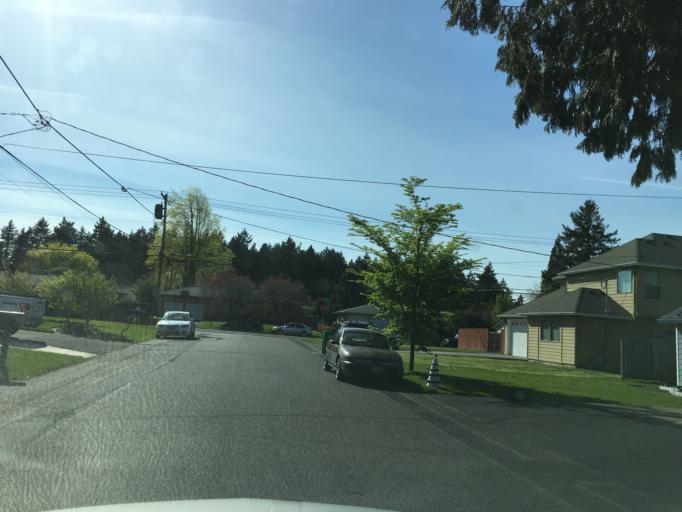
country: US
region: Oregon
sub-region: Multnomah County
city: Lents
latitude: 45.5396
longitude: -122.5263
